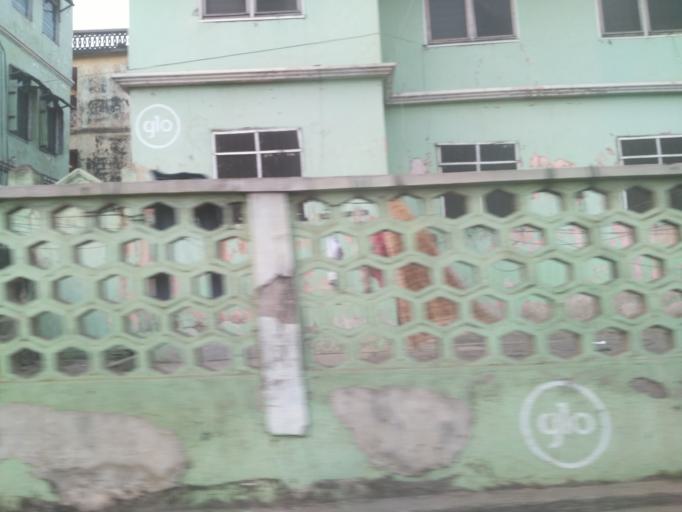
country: GH
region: Ashanti
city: Kumasi
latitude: 6.7078
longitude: -1.6067
